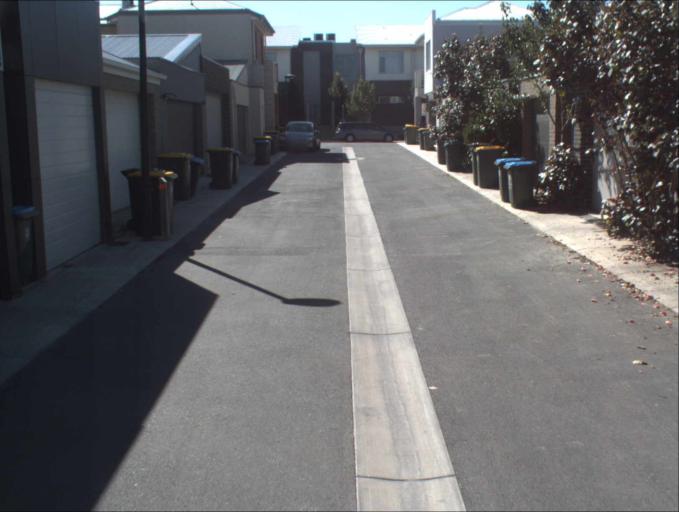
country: AU
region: South Australia
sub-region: Port Adelaide Enfield
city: Klemzig
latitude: -34.8621
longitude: 138.6340
